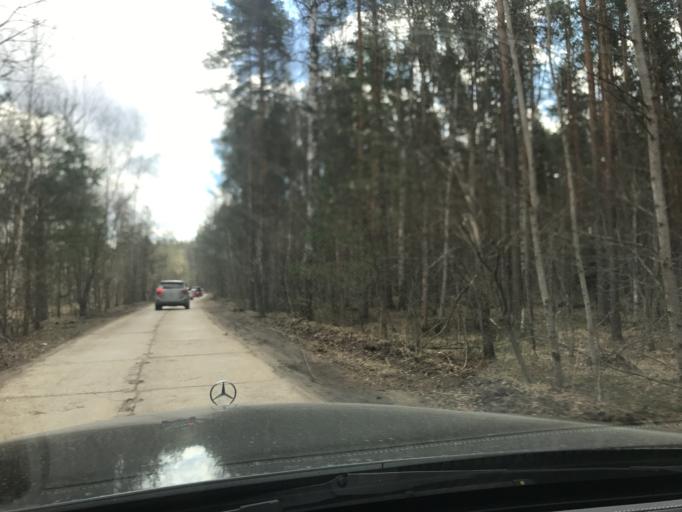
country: RU
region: Moskovskaya
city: Vereya
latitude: 55.8404
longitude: 39.1271
